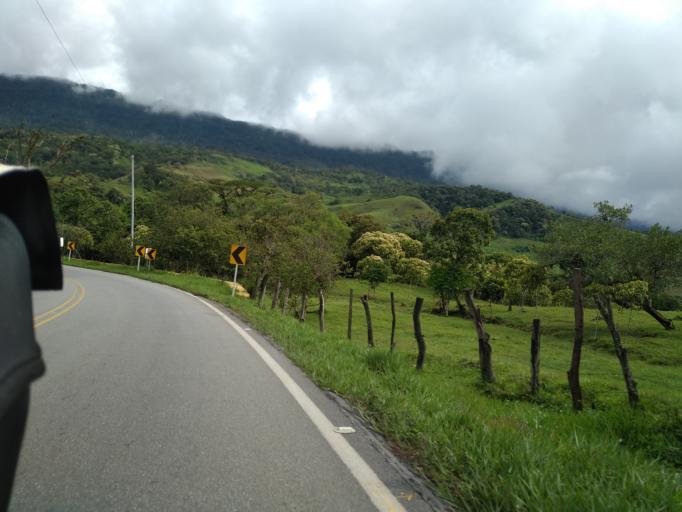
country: CO
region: Santander
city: Suaita
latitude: 6.0992
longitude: -73.3759
